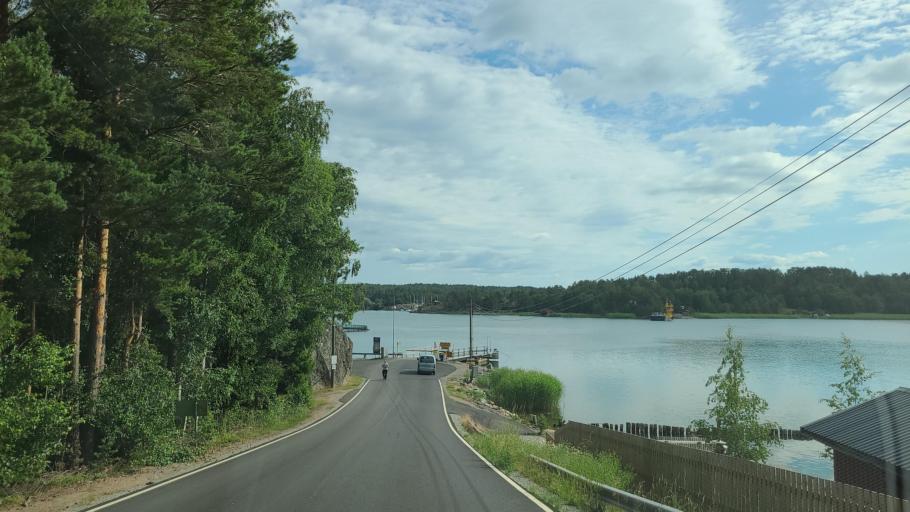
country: FI
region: Varsinais-Suomi
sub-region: Turku
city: Rymaettylae
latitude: 60.3172
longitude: 21.9632
